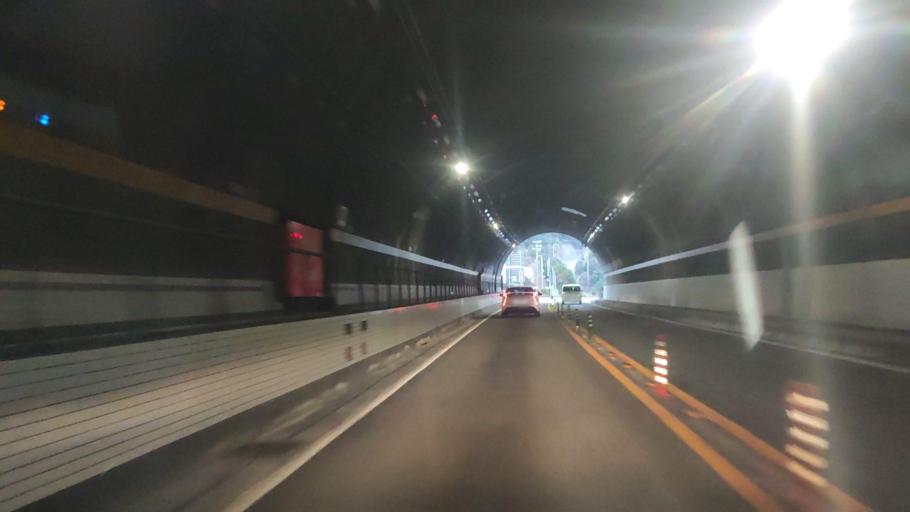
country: JP
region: Nagasaki
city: Nagasaki-shi
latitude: 32.7722
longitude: 129.8904
